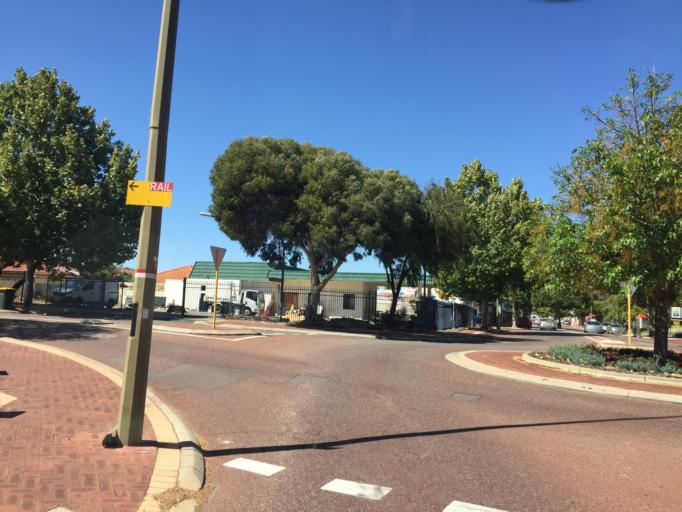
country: AU
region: Western Australia
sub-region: Victoria Park
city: Victoria Park
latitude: -31.9776
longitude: 115.9119
